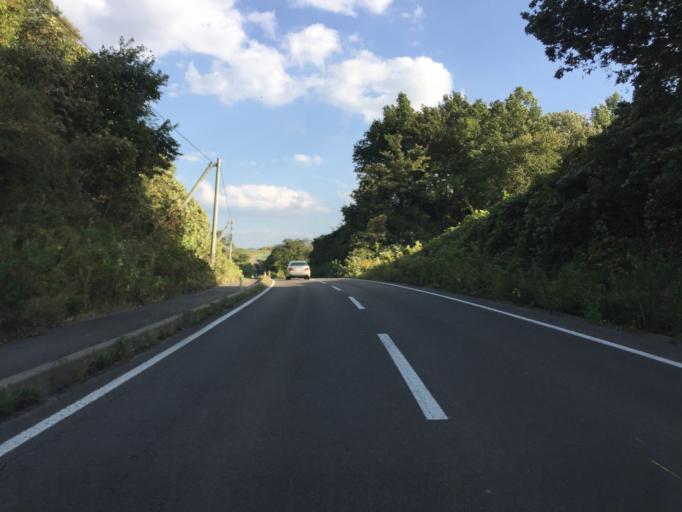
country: JP
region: Fukushima
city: Fukushima-shi
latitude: 37.6741
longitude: 140.5079
